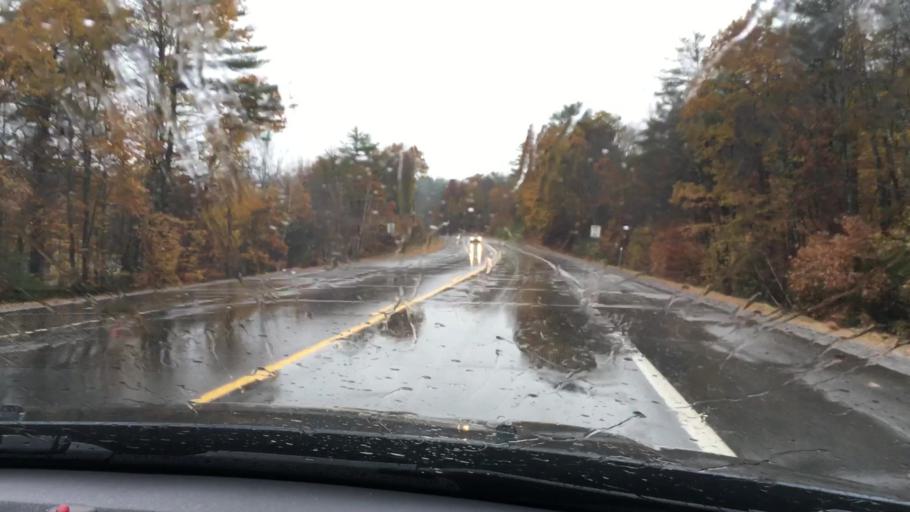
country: US
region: New Hampshire
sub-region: Grafton County
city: Ashland
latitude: 43.7081
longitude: -71.6285
